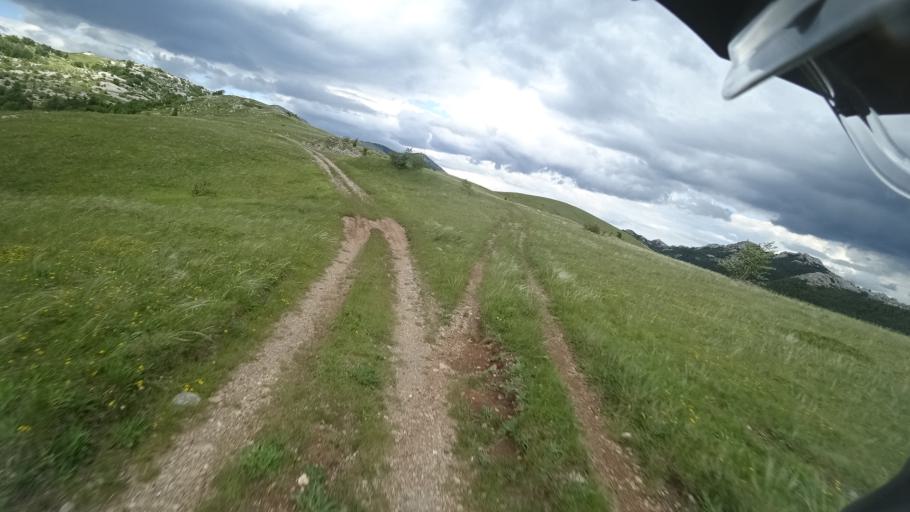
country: HR
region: Zadarska
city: Obrovac
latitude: 44.2668
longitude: 15.7356
